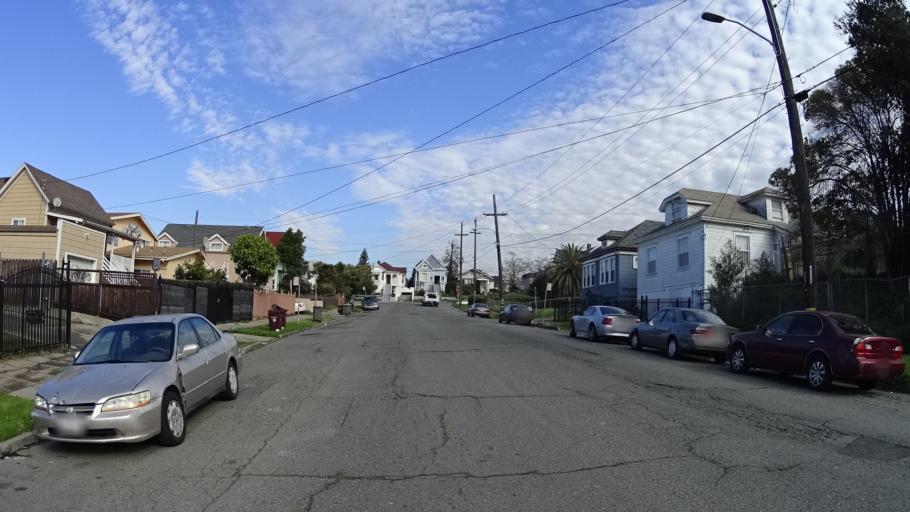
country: US
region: California
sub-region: Alameda County
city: Alameda
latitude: 37.7888
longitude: -122.2339
